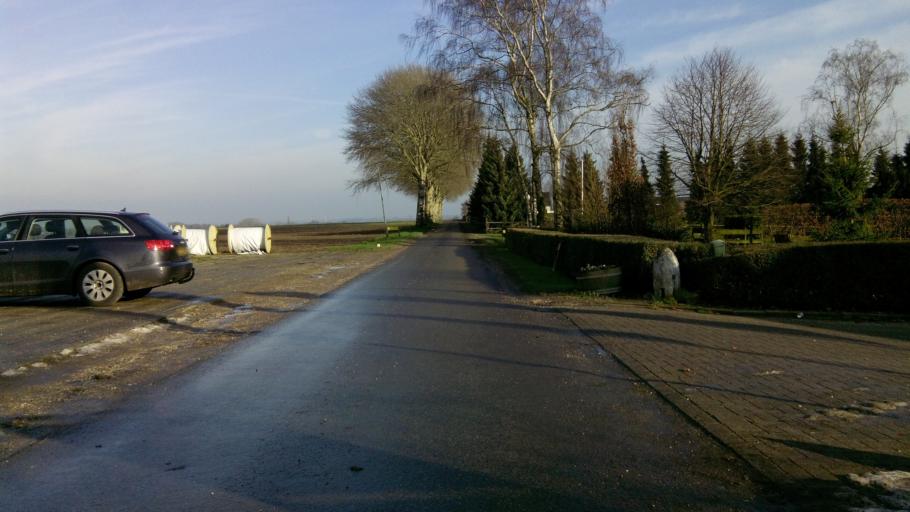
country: NL
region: Gelderland
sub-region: Gemeente Groesbeek
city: Bredeweg
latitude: 51.7601
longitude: 5.9233
